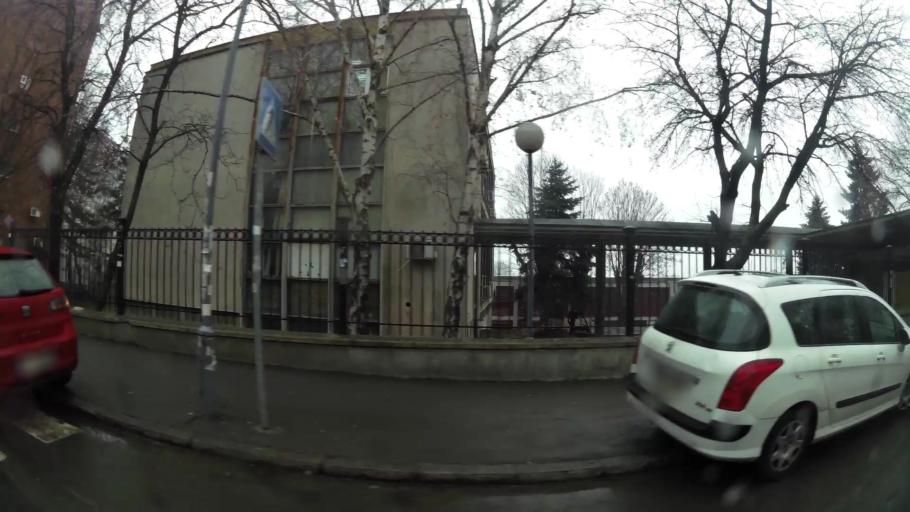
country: RS
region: Central Serbia
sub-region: Belgrade
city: Cukarica
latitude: 44.7758
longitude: 20.4116
